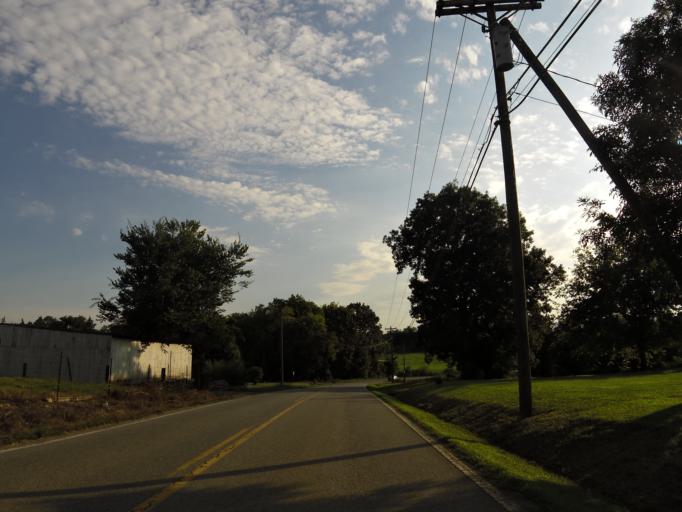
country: US
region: Tennessee
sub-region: Monroe County
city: Madisonville
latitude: 35.6010
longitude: -84.3675
